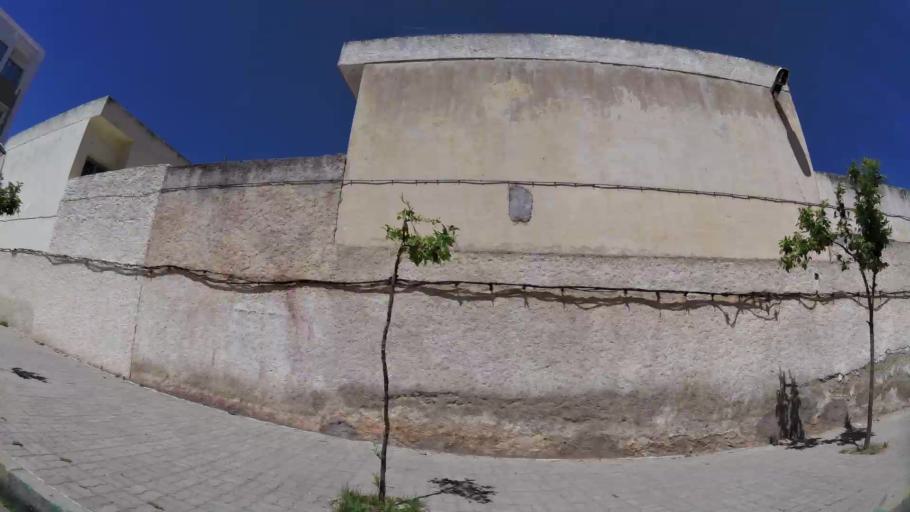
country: MA
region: Fes-Boulemane
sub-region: Fes
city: Fes
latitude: 34.0217
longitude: -5.0061
